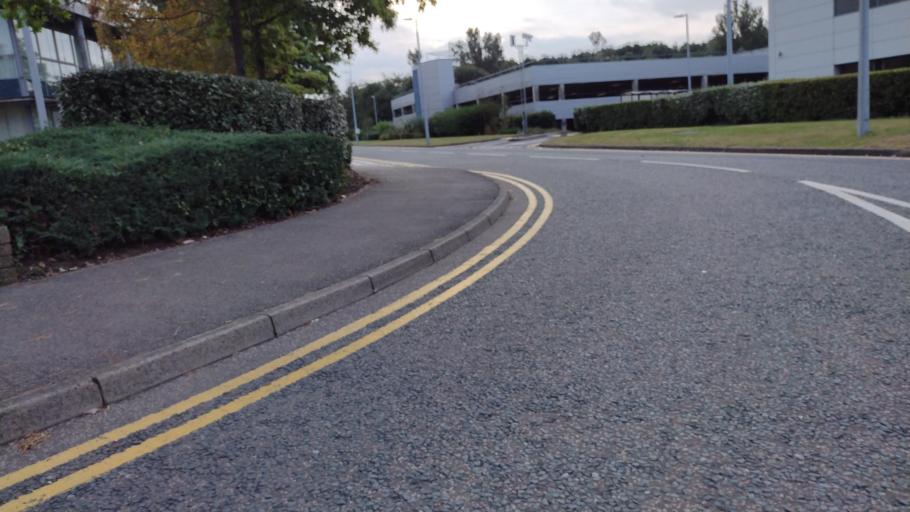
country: GB
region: England
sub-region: Wokingham
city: Winnersh
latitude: 51.4377
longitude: -0.8810
